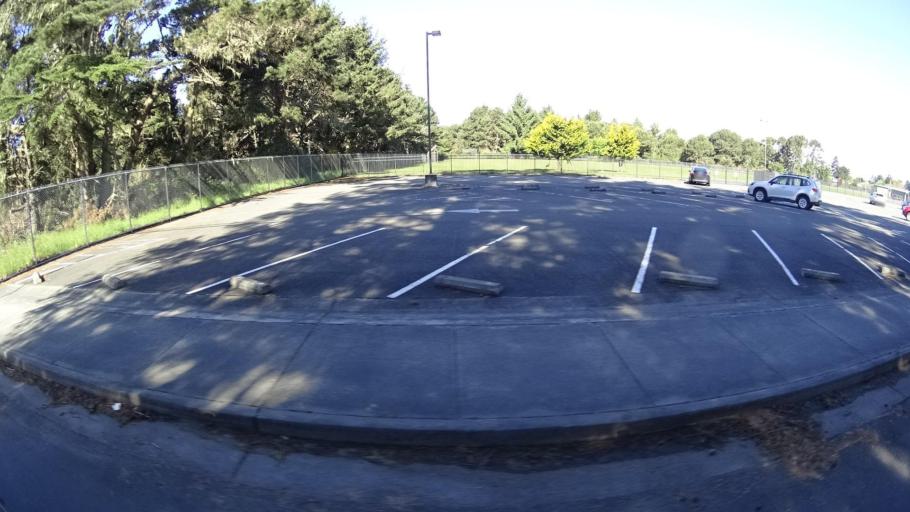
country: US
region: California
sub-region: Humboldt County
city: McKinleyville
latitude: 40.9758
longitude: -124.0959
